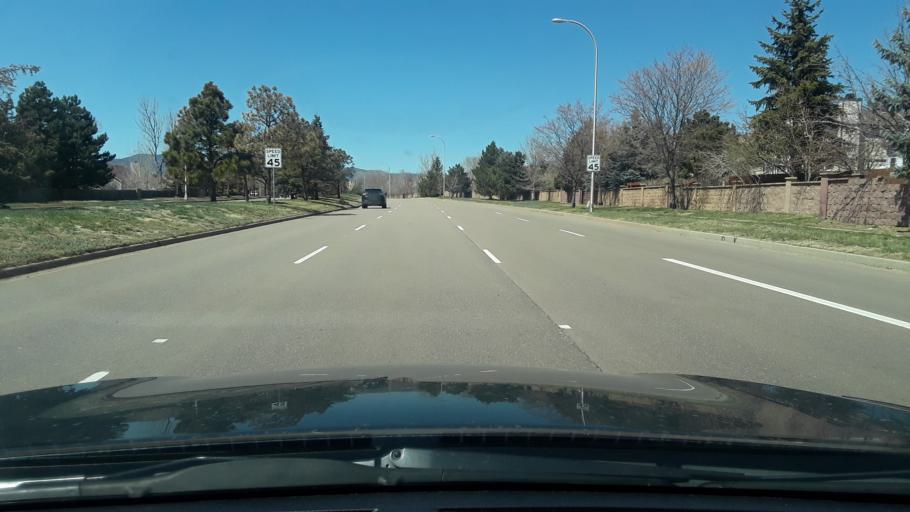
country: US
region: Colorado
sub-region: El Paso County
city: Black Forest
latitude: 38.9555
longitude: -104.7463
